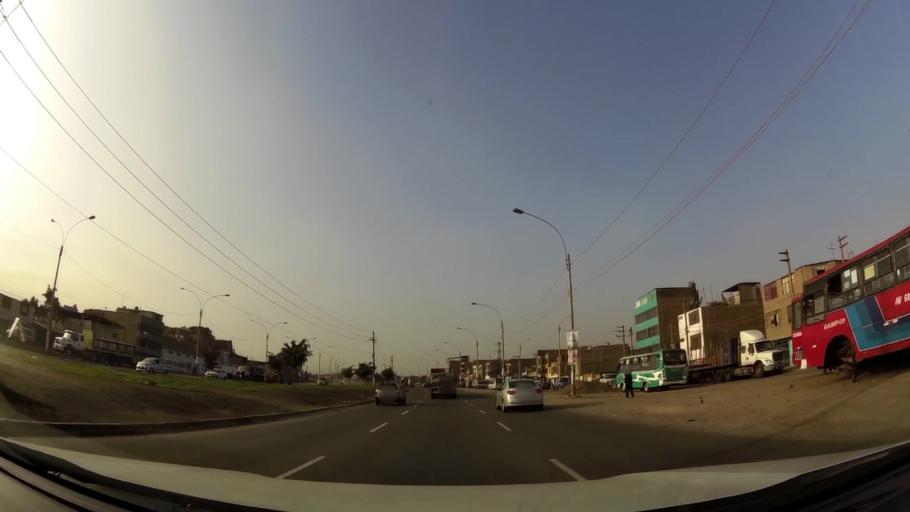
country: PE
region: Lima
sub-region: Lima
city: Independencia
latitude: -11.9710
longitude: -77.0850
